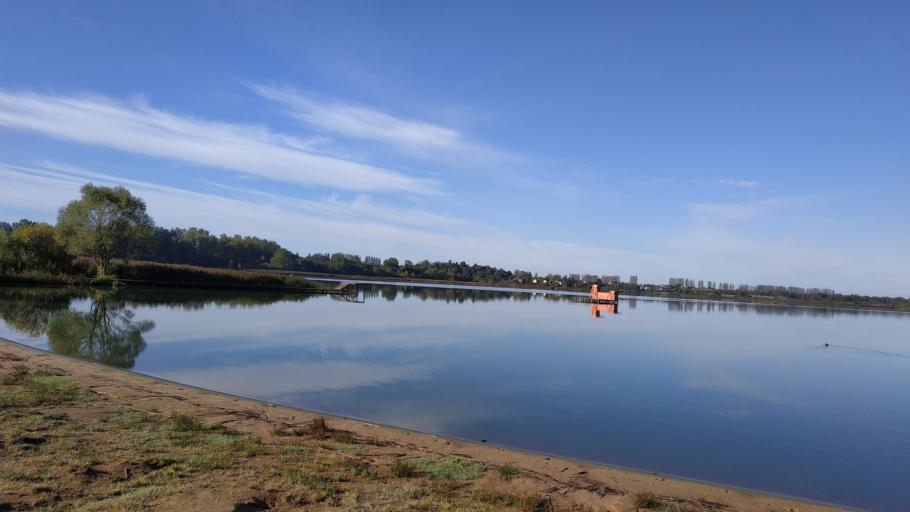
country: BY
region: Vitebsk
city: Vitebsk
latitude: 55.0898
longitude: 30.1651
